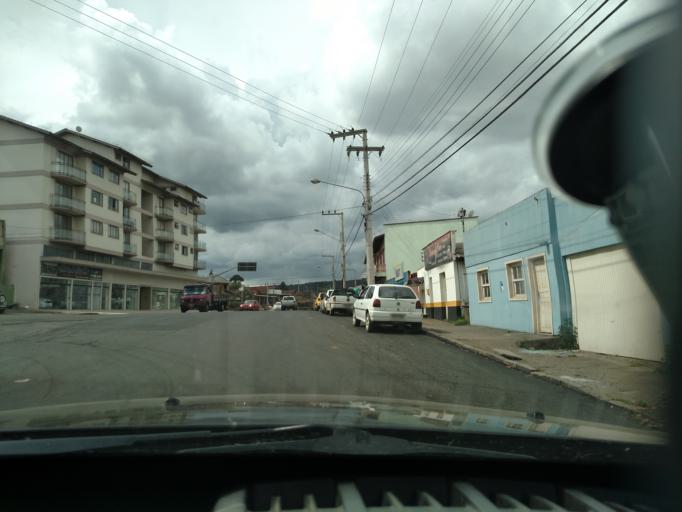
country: BR
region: Santa Catarina
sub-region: Sao Joaquim
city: Sao Joaquim
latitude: -28.2880
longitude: -49.9337
